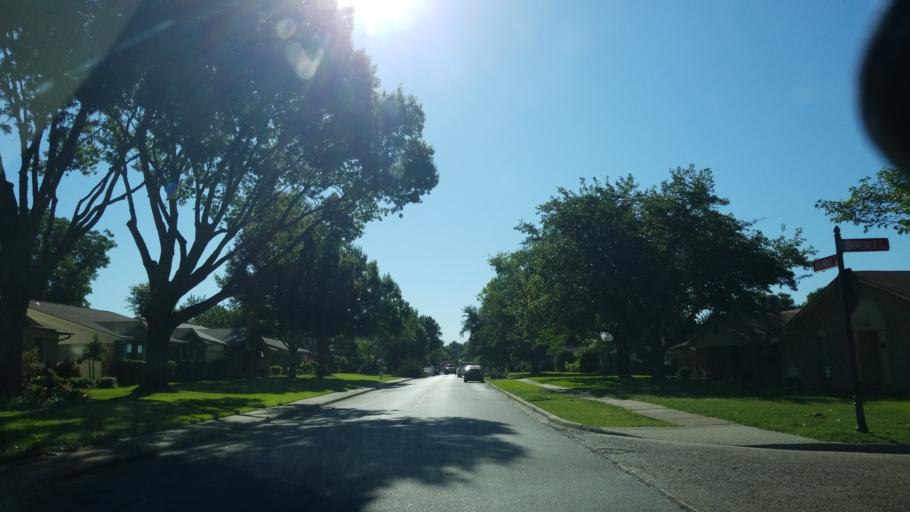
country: US
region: Texas
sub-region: Dallas County
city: Carrollton
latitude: 32.9432
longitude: -96.8882
